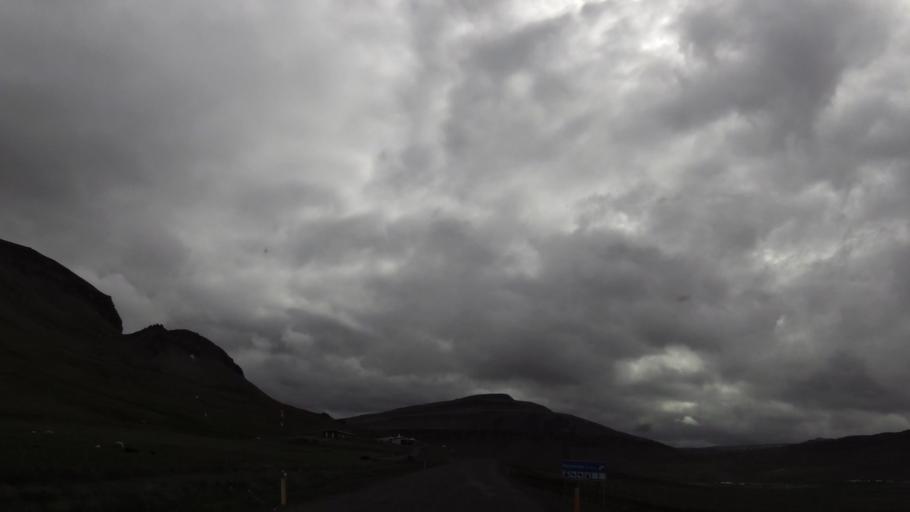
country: IS
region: West
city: Borgarnes
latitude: 65.3847
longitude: -21.8793
